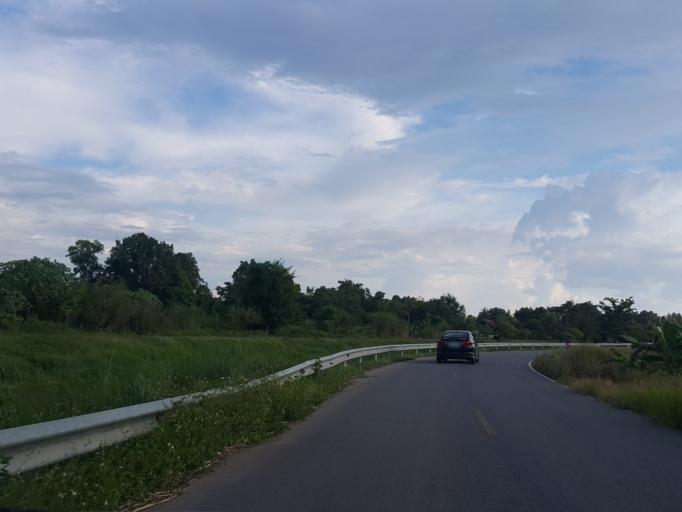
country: TH
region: Chiang Mai
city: Mae Taeng
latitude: 18.9969
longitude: 98.9811
